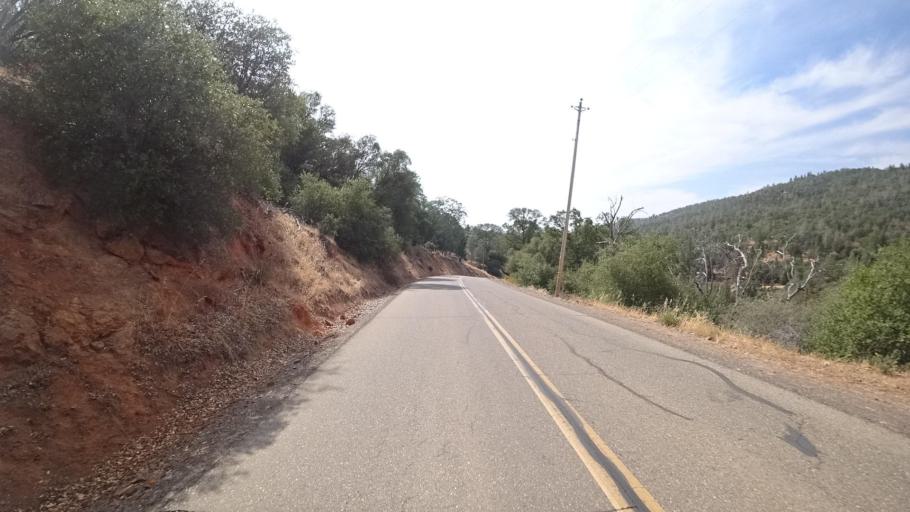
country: US
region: California
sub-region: Mariposa County
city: Mariposa
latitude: 37.5542
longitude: -120.0011
